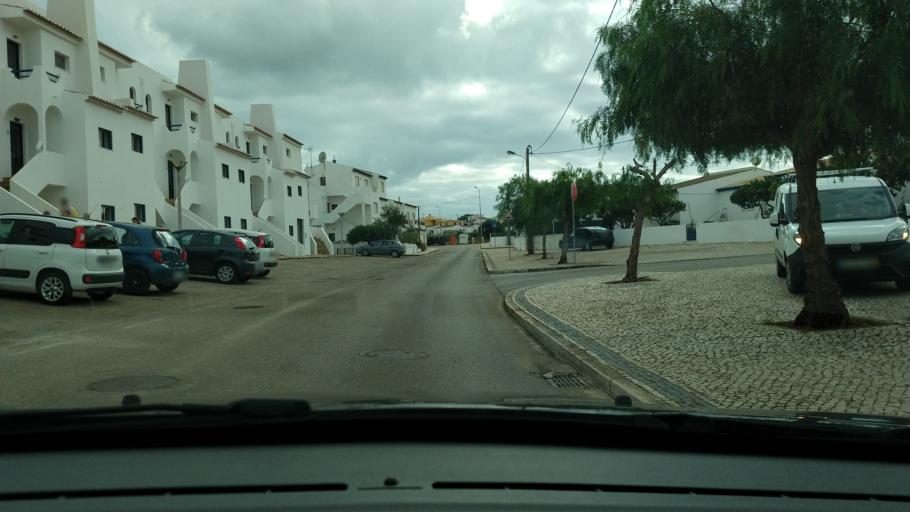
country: PT
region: Faro
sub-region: Lagos
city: Lagos
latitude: 37.0752
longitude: -8.7755
